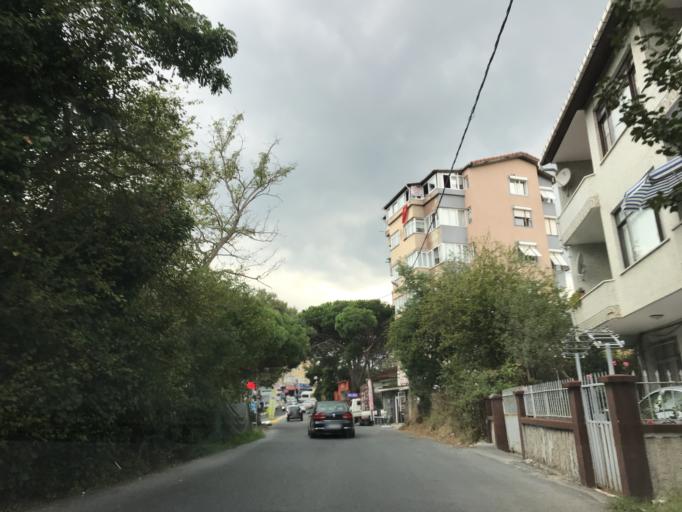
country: TR
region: Istanbul
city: Arikoey
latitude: 41.1781
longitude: 29.0515
